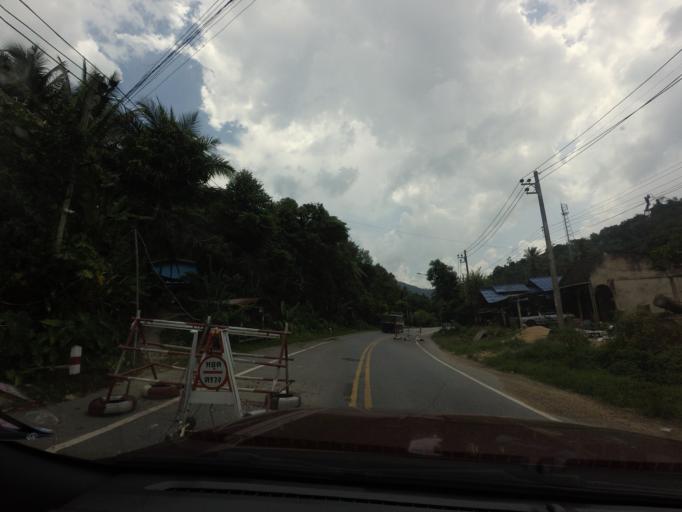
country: TH
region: Yala
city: Than To
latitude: 6.0764
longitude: 101.1897
